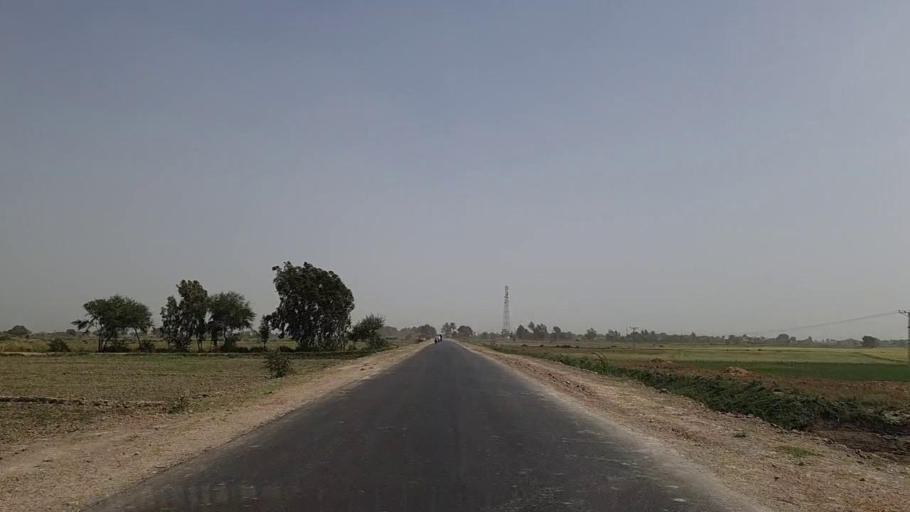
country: PK
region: Sindh
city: Tando Bago
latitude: 24.8195
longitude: 68.9043
